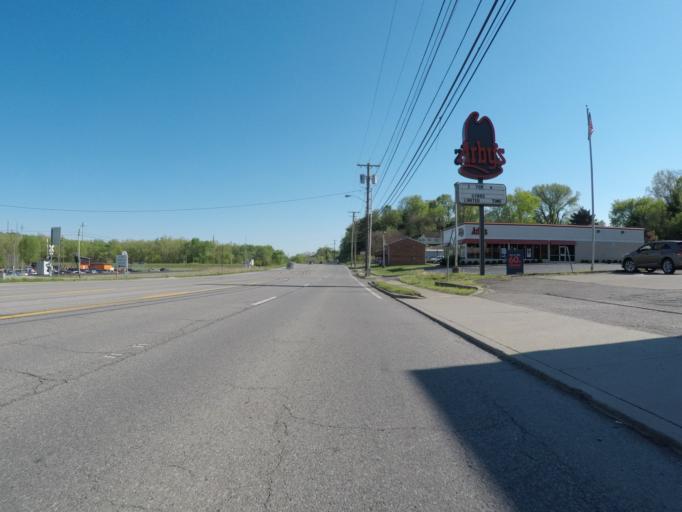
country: US
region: Kentucky
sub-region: Boyd County
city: Catlettsburg
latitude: 38.4010
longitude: -82.6010
